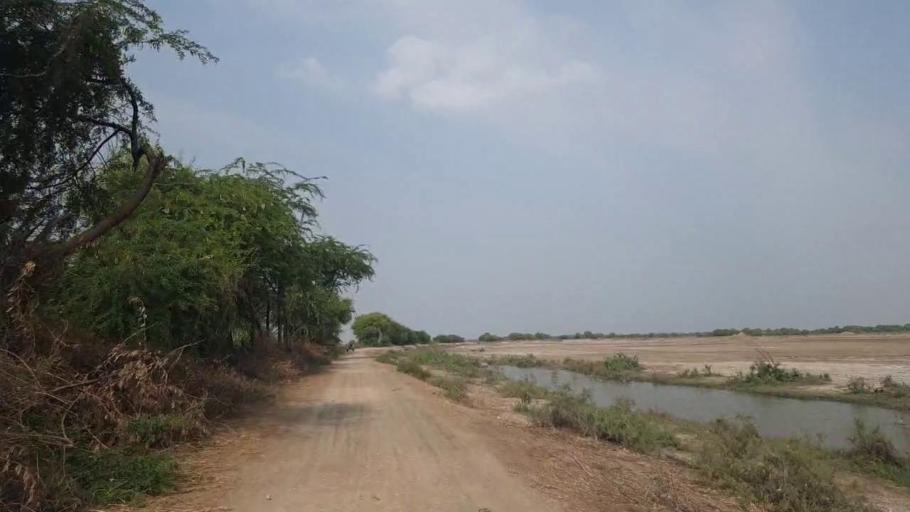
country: PK
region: Sindh
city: Badin
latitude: 24.5519
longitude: 68.7310
